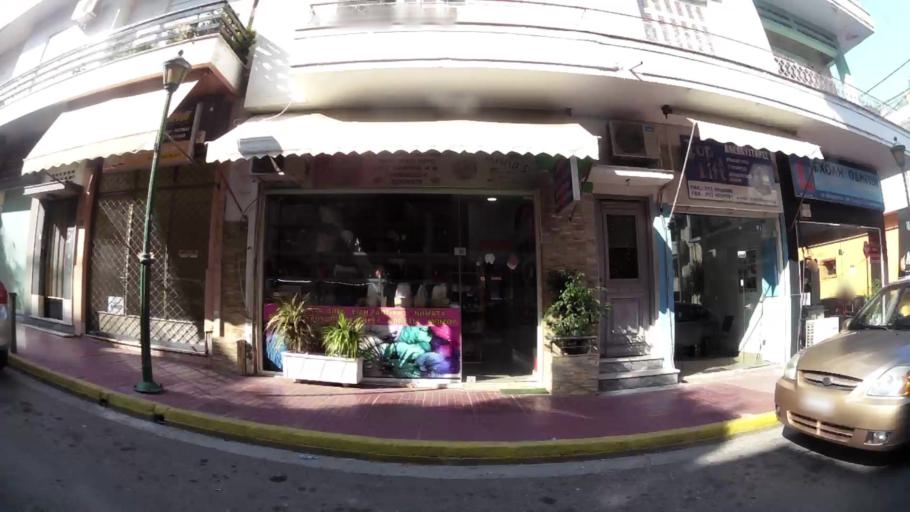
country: GR
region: Attica
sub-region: Nomos Piraios
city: Drapetsona
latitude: 37.9512
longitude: 23.6262
